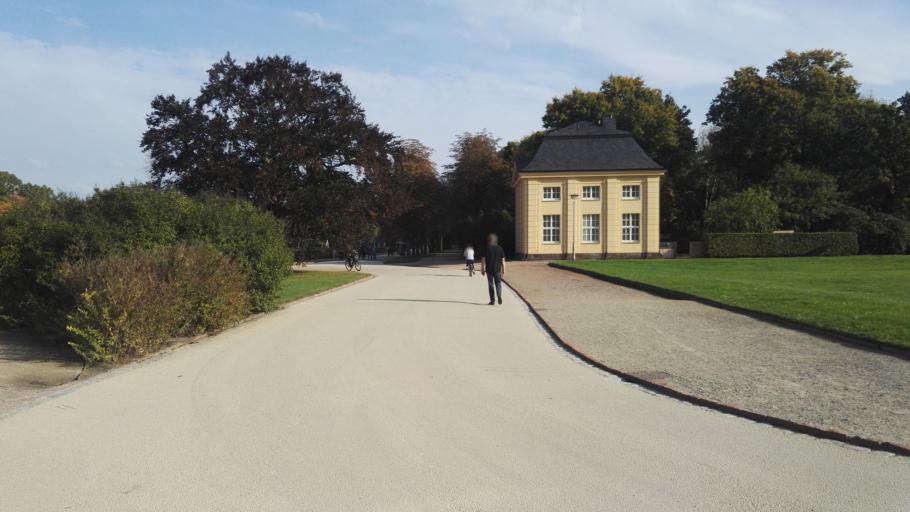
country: DE
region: Saxony
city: Dresden
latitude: 51.0374
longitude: 13.7625
